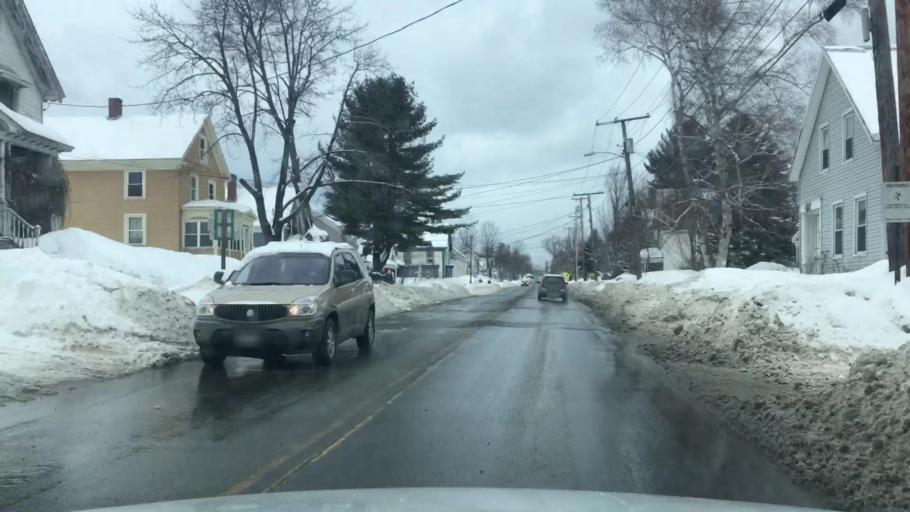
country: US
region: Maine
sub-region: Somerset County
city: Skowhegan
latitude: 44.7682
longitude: -69.7164
